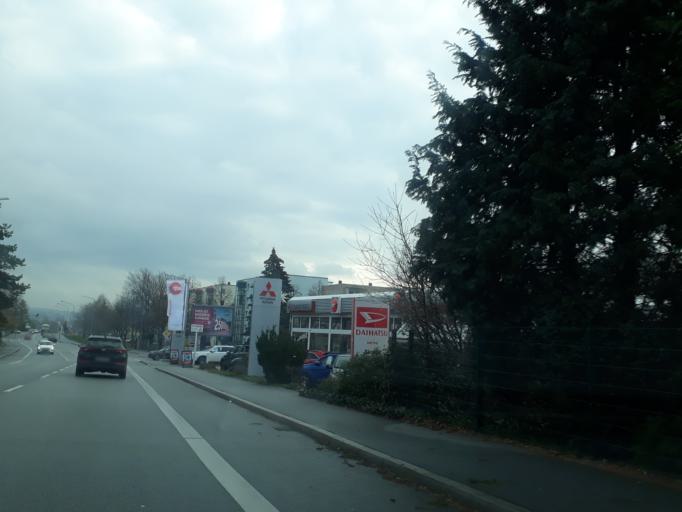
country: DE
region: Saxony
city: Bautzen
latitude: 51.1779
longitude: 14.4548
